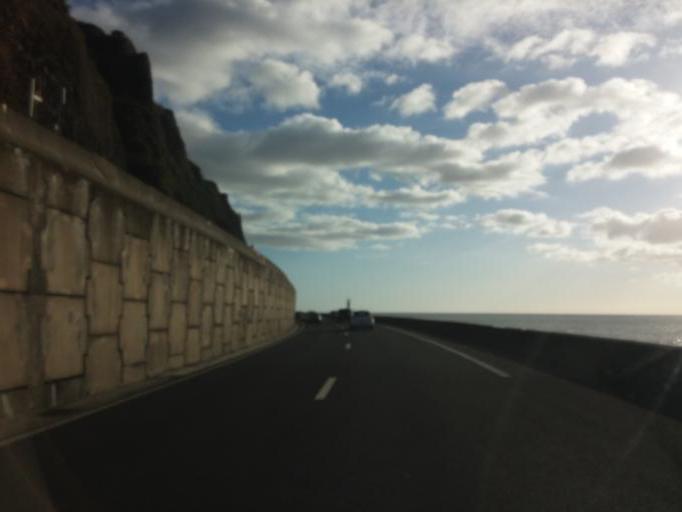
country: RE
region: Reunion
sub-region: Reunion
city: Saint-Denis
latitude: -20.8745
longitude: 55.4219
